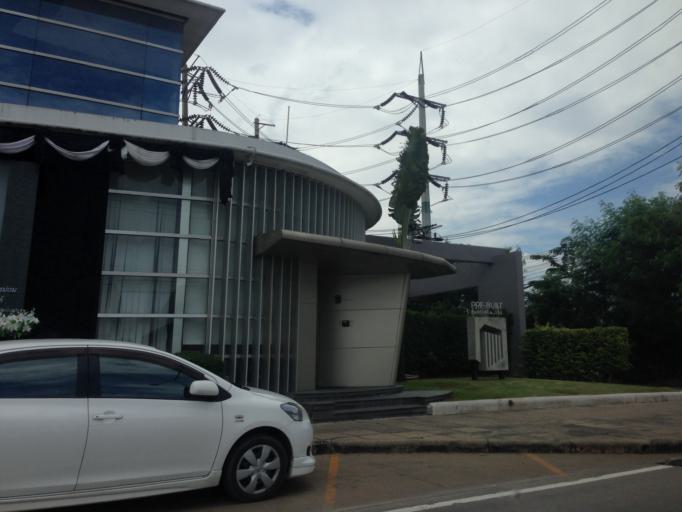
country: TH
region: Nonthaburi
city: Pak Kret
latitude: 13.9290
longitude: 100.5316
